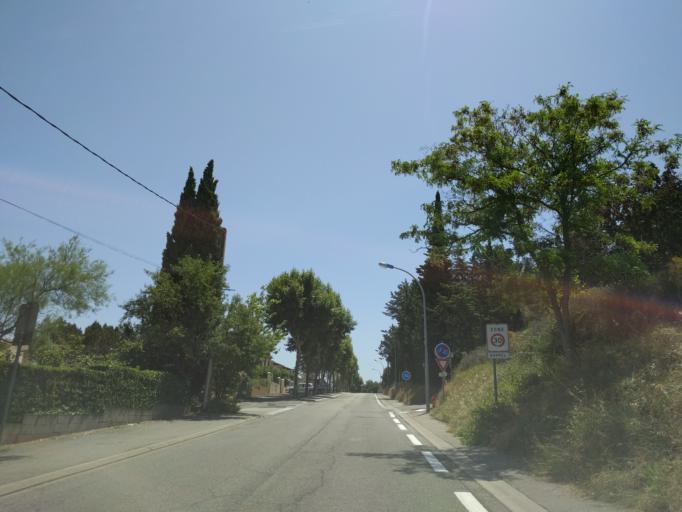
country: FR
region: Languedoc-Roussillon
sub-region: Departement de l'Aude
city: Palaja
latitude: 43.2045
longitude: 2.3915
